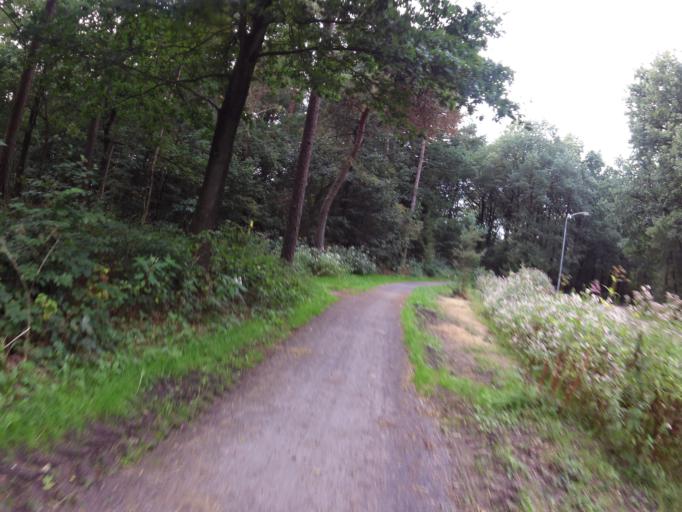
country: NL
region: Drenthe
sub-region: Gemeente Westerveld
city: Dwingeloo
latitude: 52.8191
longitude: 6.3698
